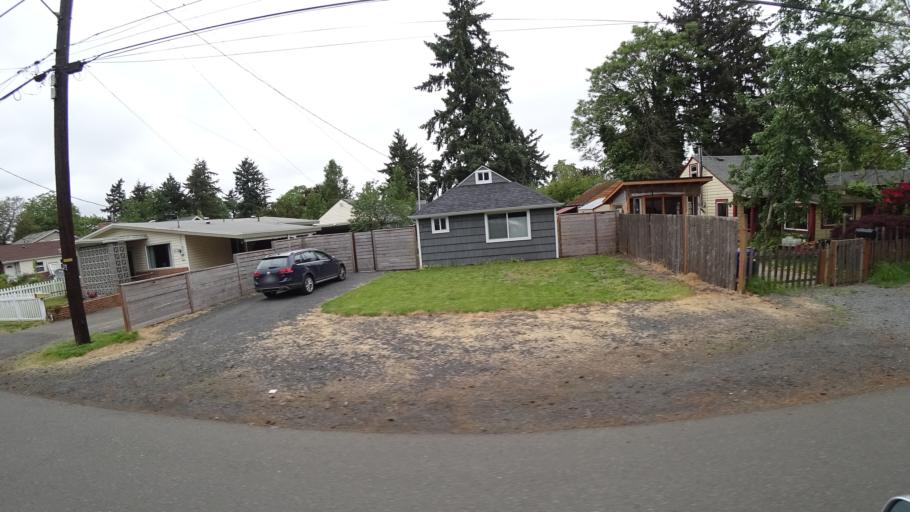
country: US
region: Oregon
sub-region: Multnomah County
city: Portland
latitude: 45.5584
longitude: -122.6128
